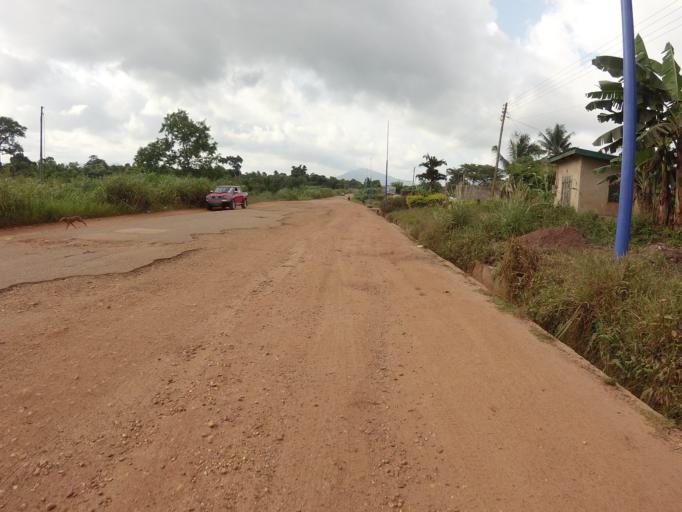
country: GH
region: Volta
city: Hohoe
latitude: 7.1248
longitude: 0.4601
